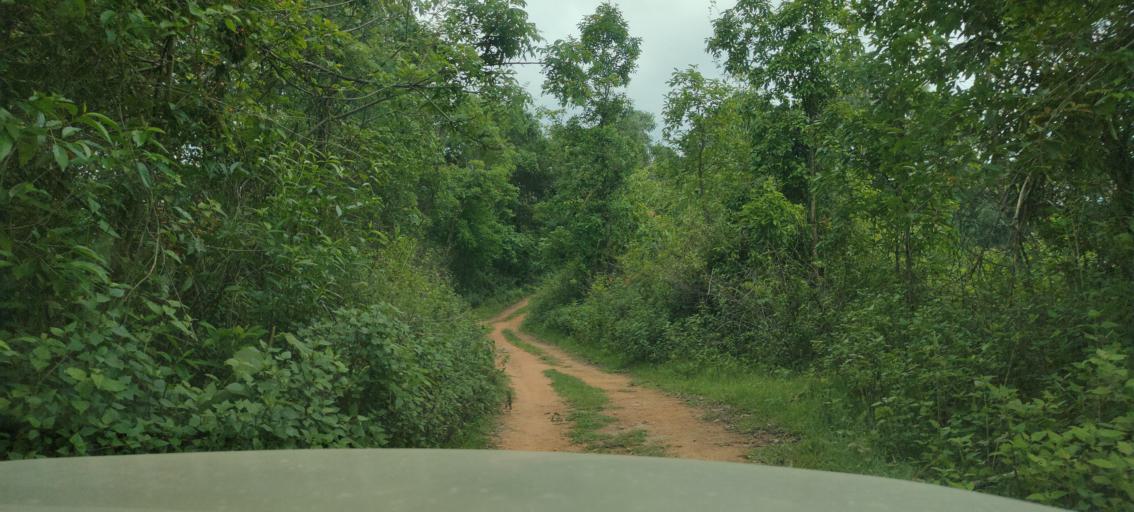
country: LA
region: Loungnamtha
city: Muang Nale
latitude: 20.4243
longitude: 101.4672
